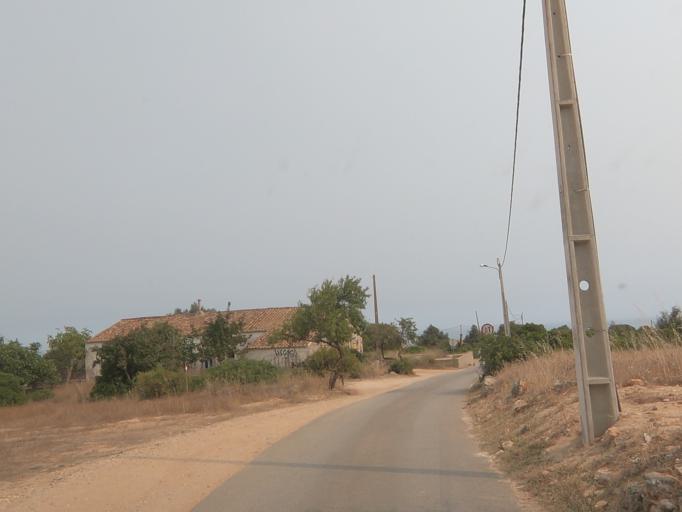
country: PT
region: Faro
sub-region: Lagoa
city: Carvoeiro
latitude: 37.0975
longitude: -8.4099
